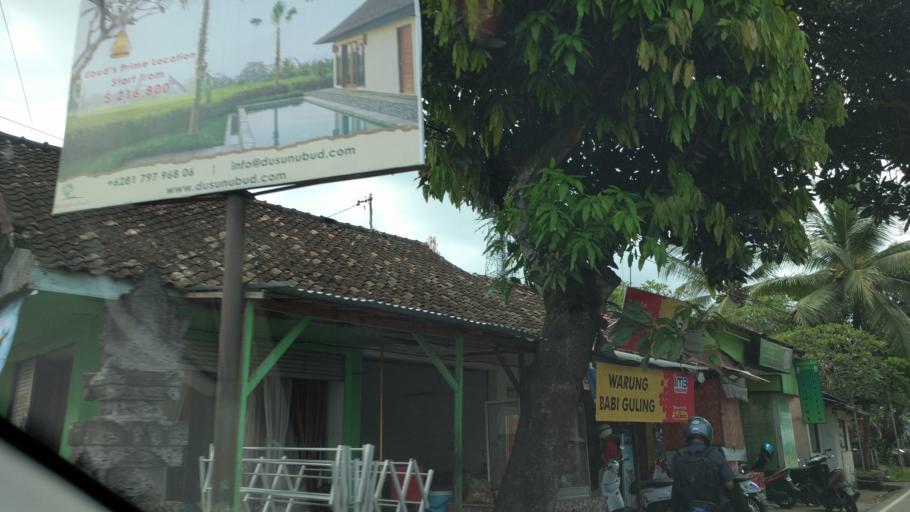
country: ID
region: Bali
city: Banjar Tebongkang
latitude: -8.5275
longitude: 115.2435
